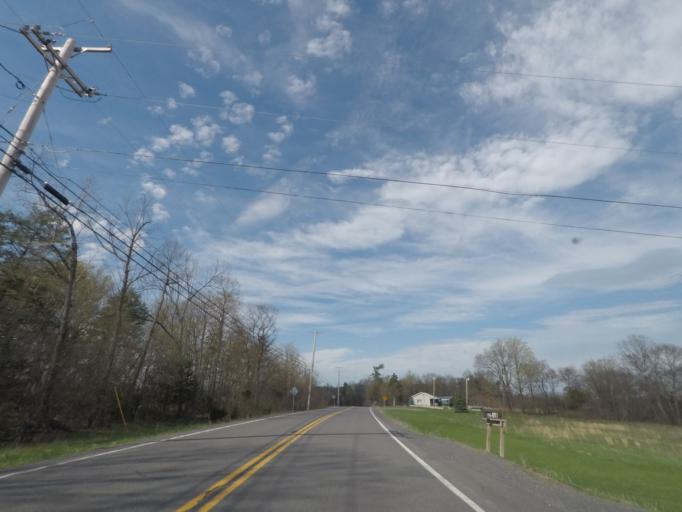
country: US
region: New York
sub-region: Albany County
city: Voorheesville
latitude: 42.5674
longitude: -73.9535
